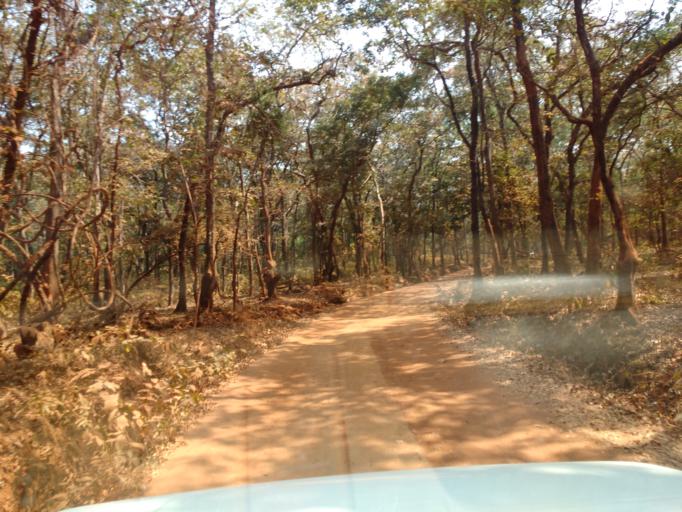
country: IN
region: Goa
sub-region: South Goa
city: Sanguem
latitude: 15.3413
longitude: 74.2565
